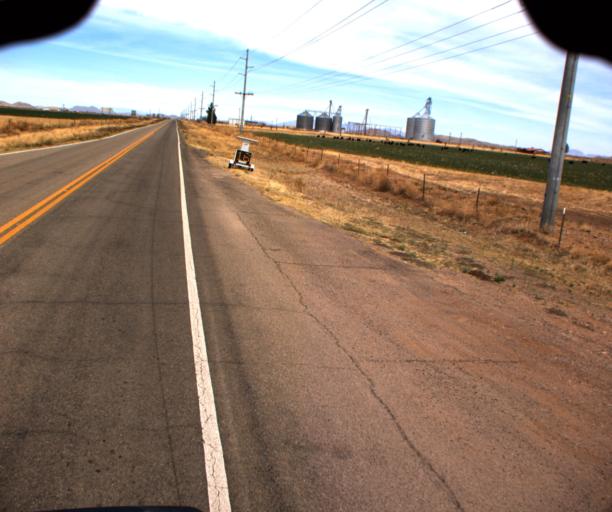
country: US
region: Arizona
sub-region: Cochise County
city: Tombstone
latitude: 31.7593
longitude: -109.6895
